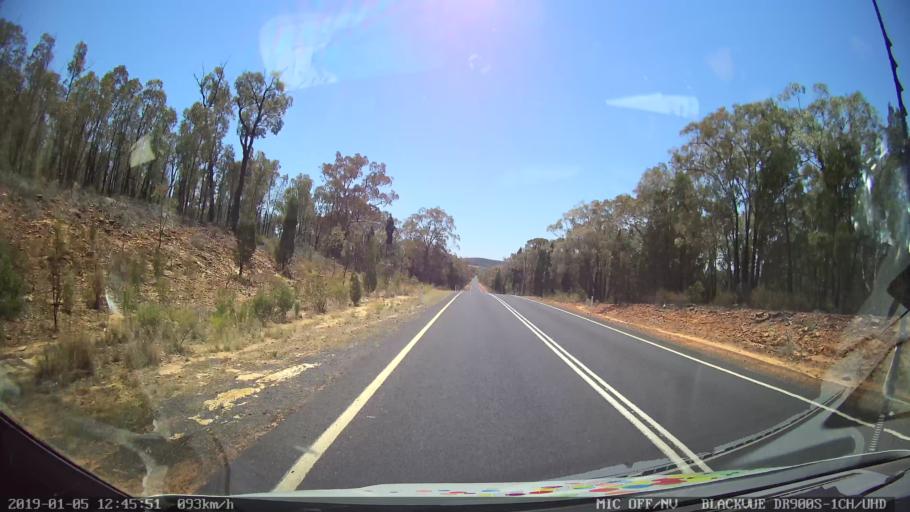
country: AU
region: New South Wales
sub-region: Warrumbungle Shire
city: Coonabarabran
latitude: -31.1238
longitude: 149.5551
